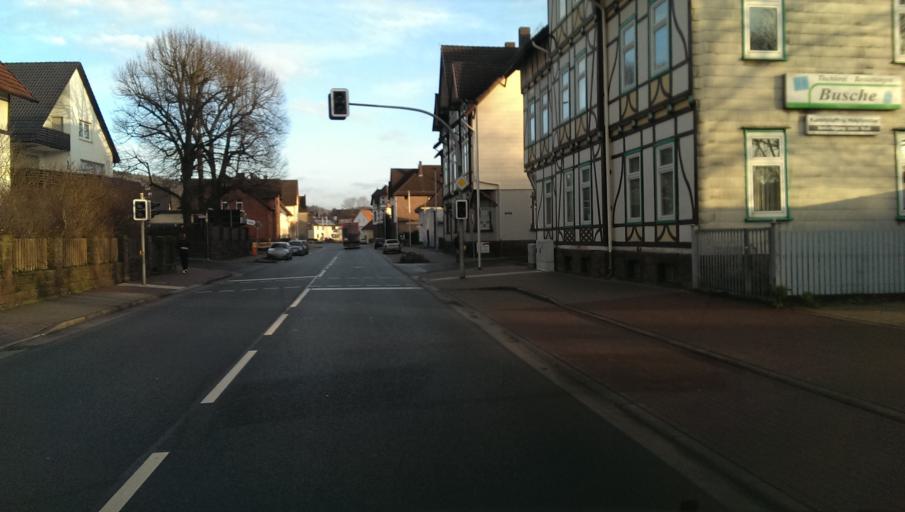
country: DE
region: Lower Saxony
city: Stadtoldendorf
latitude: 51.8819
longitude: 9.6269
